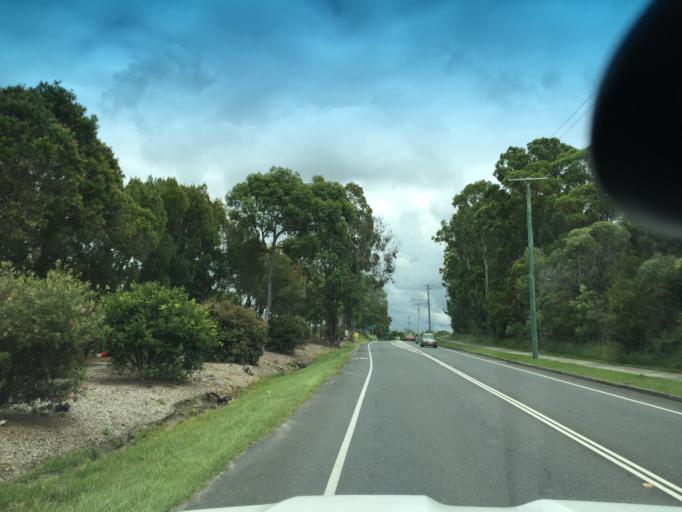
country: AU
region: Queensland
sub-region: Moreton Bay
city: Morayfield
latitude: -27.1090
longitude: 152.9722
